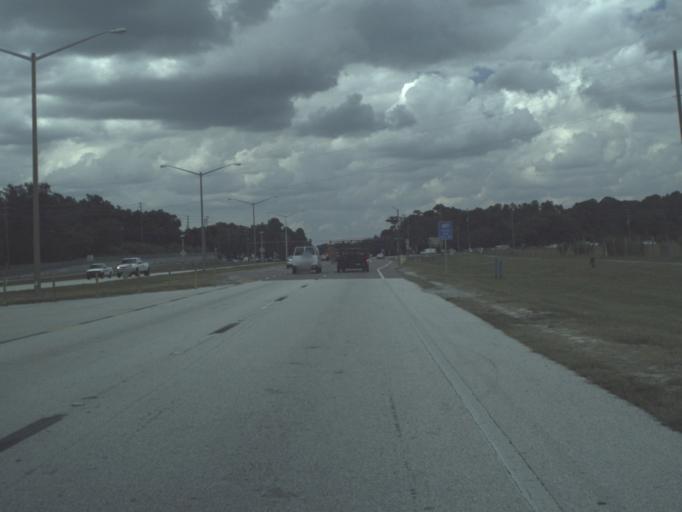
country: US
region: Florida
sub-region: Pinellas County
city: East Lake
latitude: 28.1460
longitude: -82.6956
